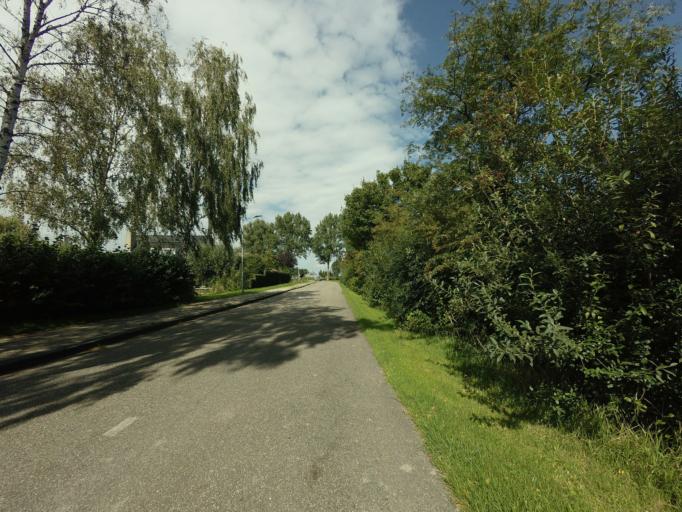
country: NL
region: Friesland
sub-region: Sudwest Fryslan
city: IJlst
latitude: 53.0090
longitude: 5.6335
